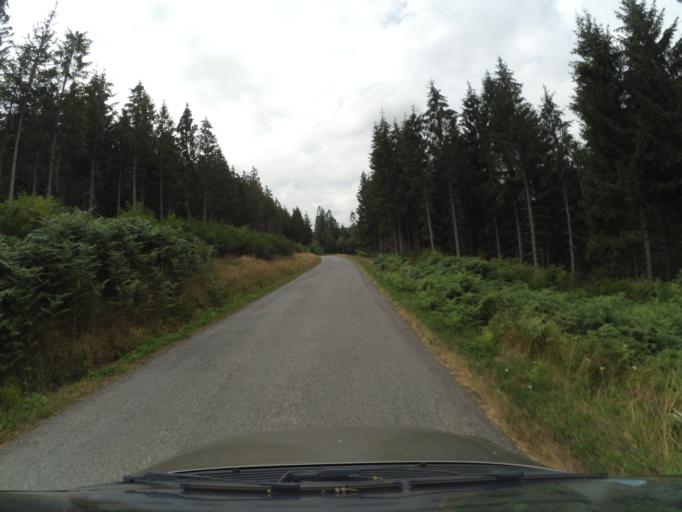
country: FR
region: Limousin
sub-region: Departement de la Correze
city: Meymac
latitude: 45.6612
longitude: 2.1124
